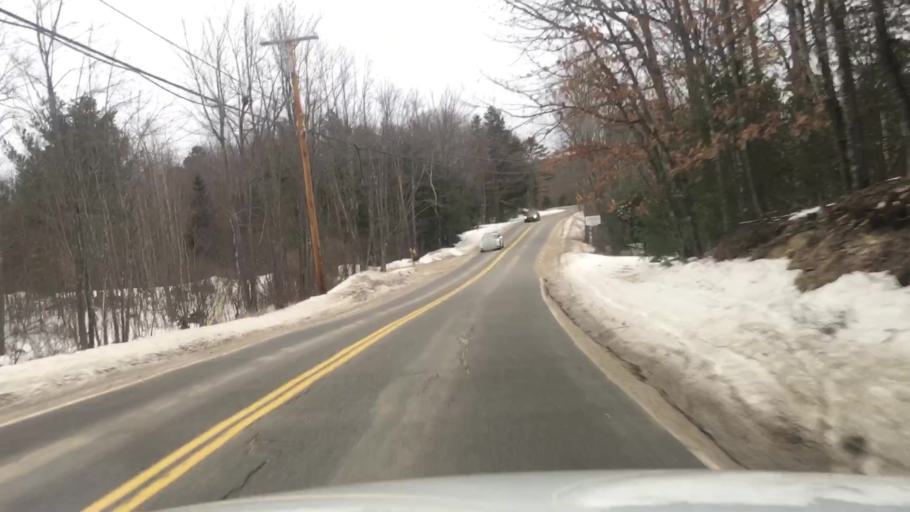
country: US
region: Maine
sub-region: York County
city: Newfield
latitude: 43.6266
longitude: -70.8394
